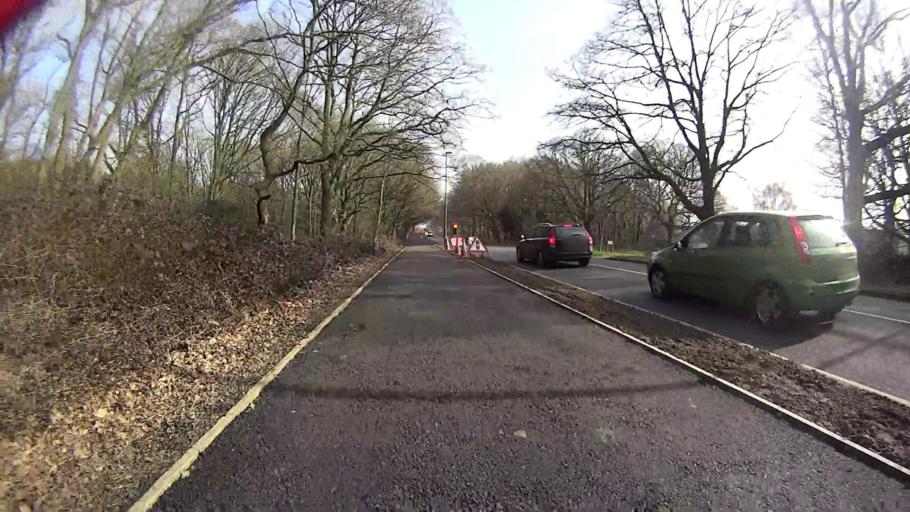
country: GB
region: England
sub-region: Surrey
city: Reigate
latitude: 51.2221
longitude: -0.1903
